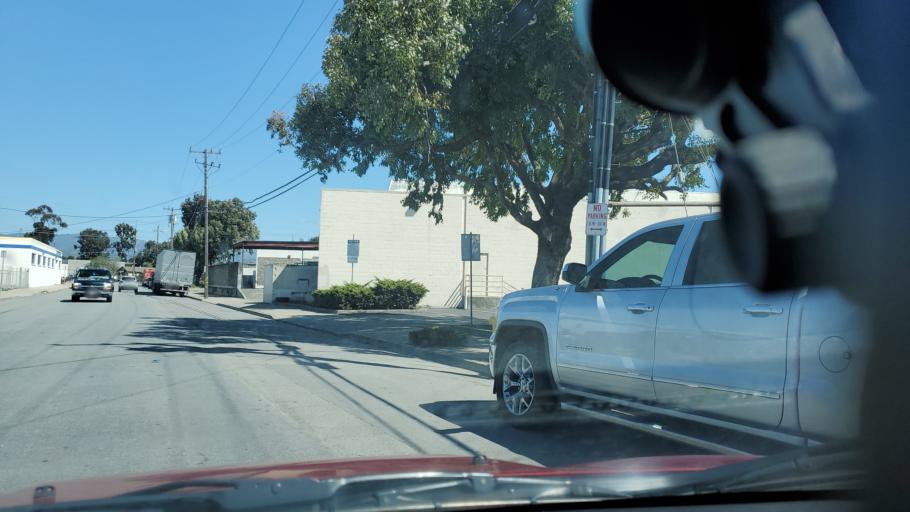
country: US
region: California
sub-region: Monterey County
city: Salinas
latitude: 36.6755
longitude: -121.6444
